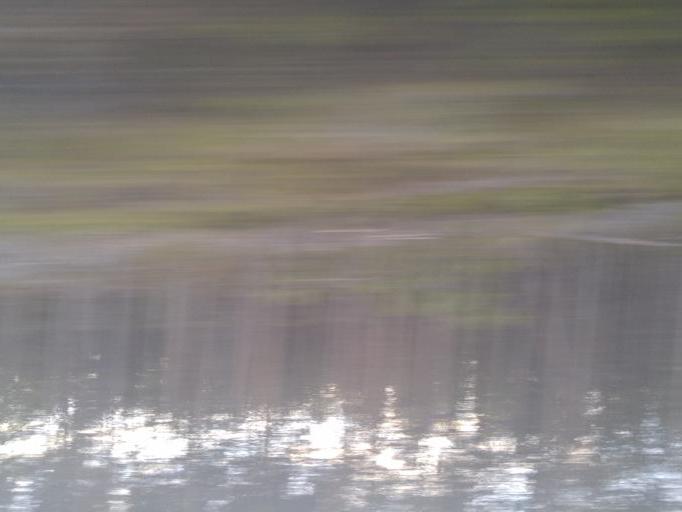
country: NO
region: Oppland
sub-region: Dovre
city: Dovre
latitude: 61.9437
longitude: 9.3006
